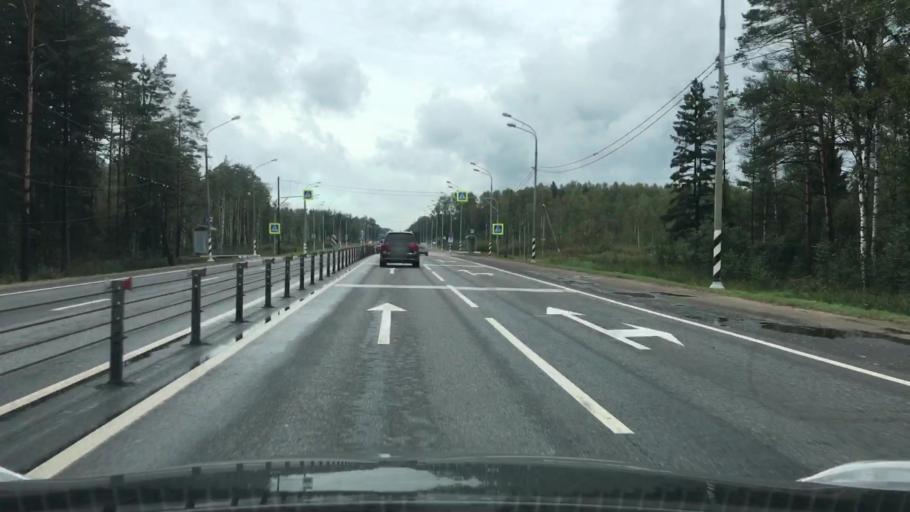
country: RU
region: Moskovskaya
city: Reshetnikovo
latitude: 56.4004
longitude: 36.6533
